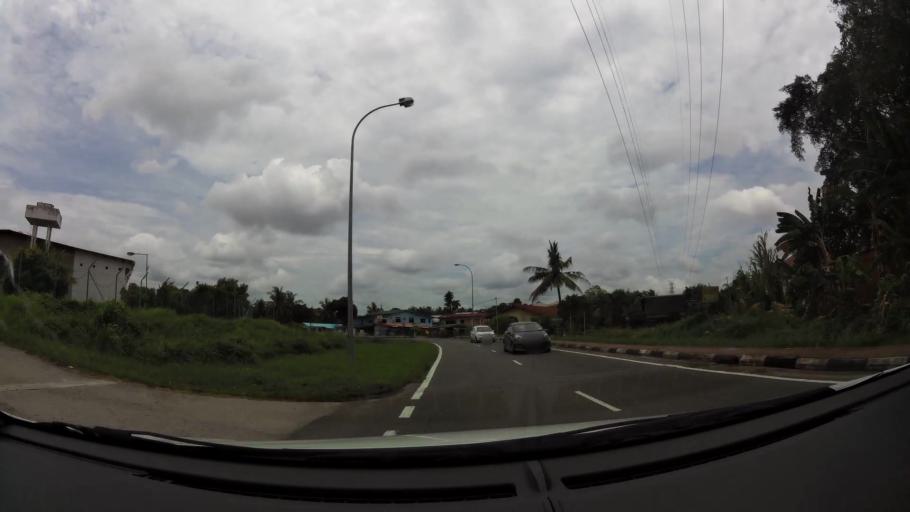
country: BN
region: Brunei and Muara
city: Bandar Seri Begawan
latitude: 4.9112
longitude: 114.9129
